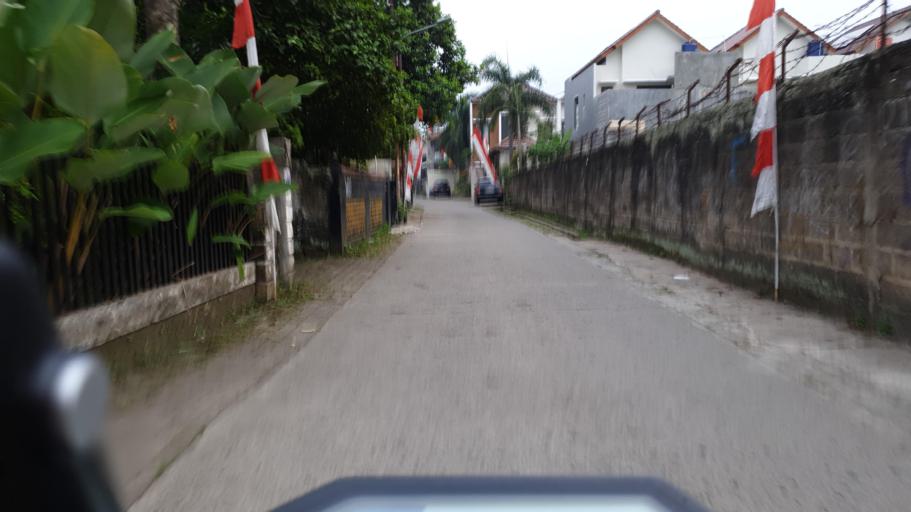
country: ID
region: West Java
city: Pamulang
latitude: -6.3190
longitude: 106.7705
